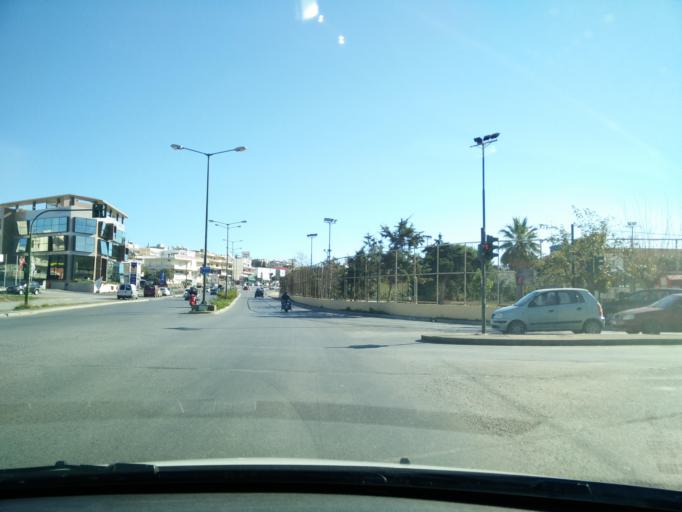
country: GR
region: Crete
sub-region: Nomos Irakleiou
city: Nea Alikarnassos
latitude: 35.3367
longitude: 25.1550
